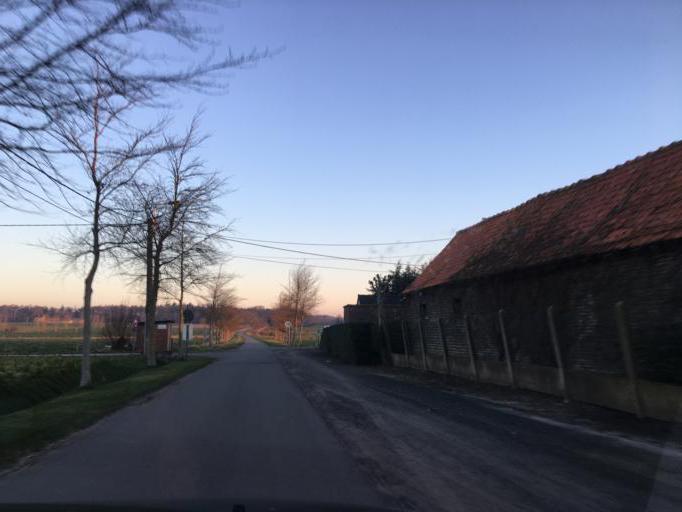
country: BE
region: Flanders
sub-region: Provincie Oost-Vlaanderen
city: Aalter
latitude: 51.1368
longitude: 3.4844
